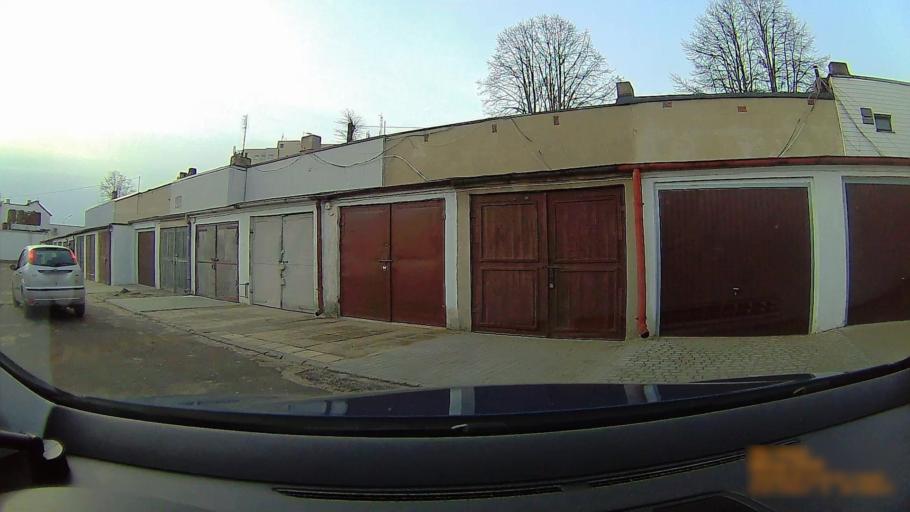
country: PL
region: Greater Poland Voivodeship
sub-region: Konin
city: Konin
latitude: 52.2317
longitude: 18.2621
